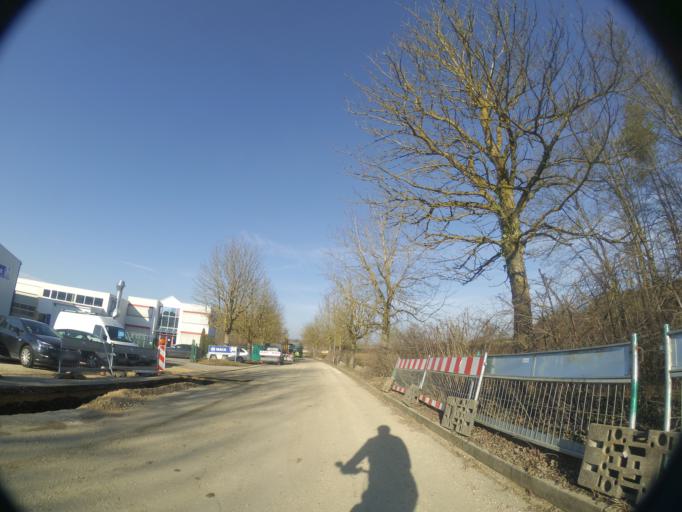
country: DE
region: Baden-Wuerttemberg
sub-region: Tuebingen Region
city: Dornstadt
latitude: 48.4734
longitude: 9.9400
